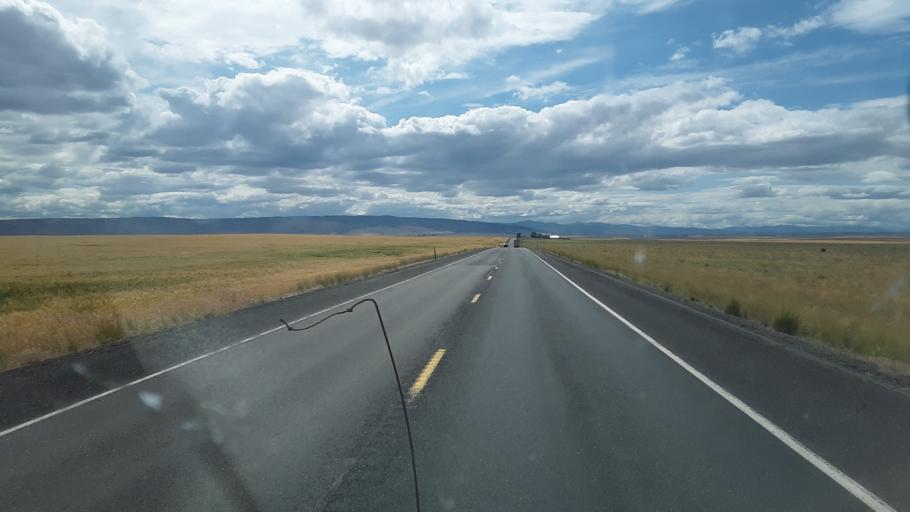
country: US
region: Washington
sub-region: Douglas County
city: Waterville
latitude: 47.6128
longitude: -119.8989
